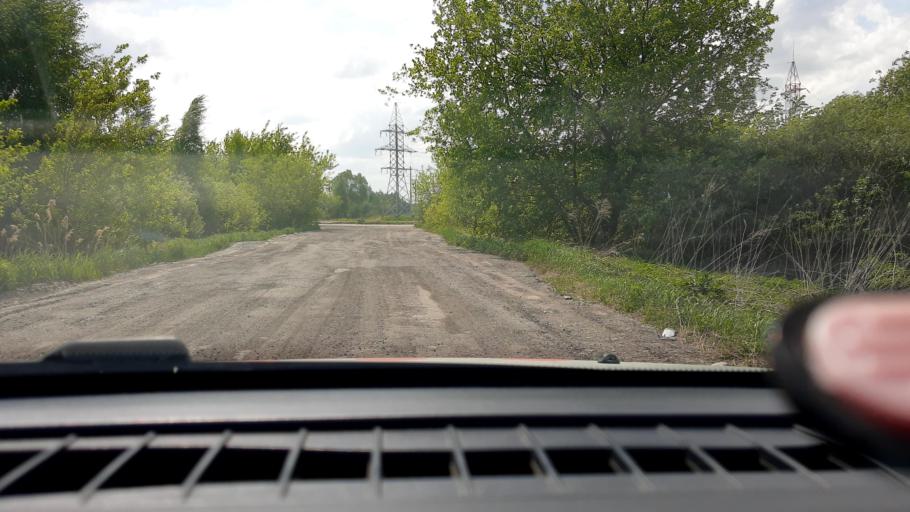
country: RU
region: Nizjnij Novgorod
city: Kstovo
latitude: 56.1260
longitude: 44.1250
